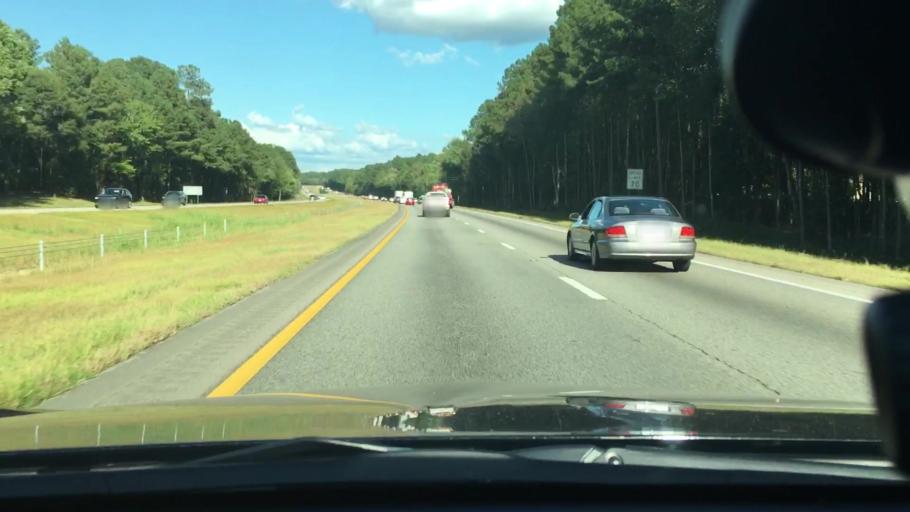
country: US
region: North Carolina
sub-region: Wake County
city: Wendell
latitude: 35.8272
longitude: -78.3630
